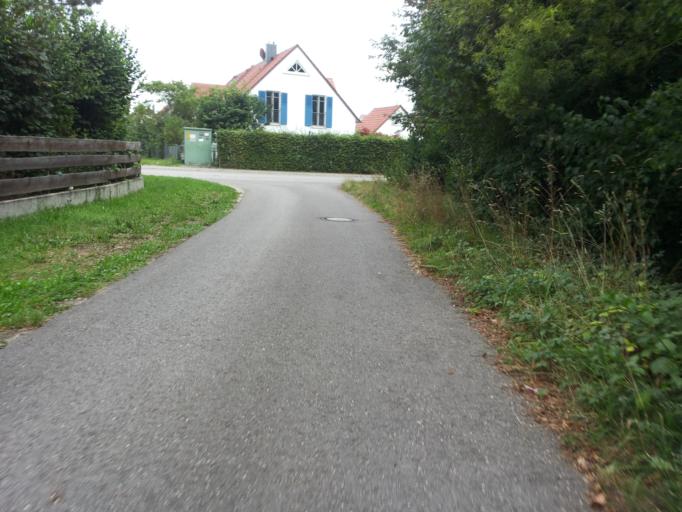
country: DE
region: Bavaria
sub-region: Upper Bavaria
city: Weichering
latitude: 48.7493
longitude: 11.3462
